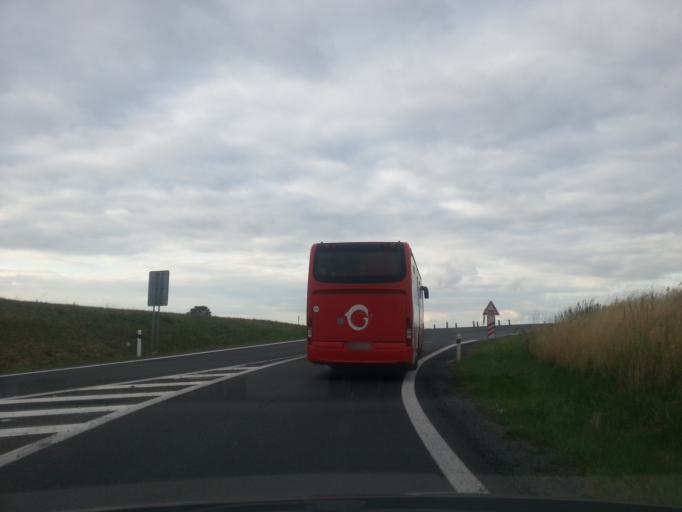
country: CZ
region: Central Bohemia
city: Unhost'
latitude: 50.1020
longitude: 14.1382
